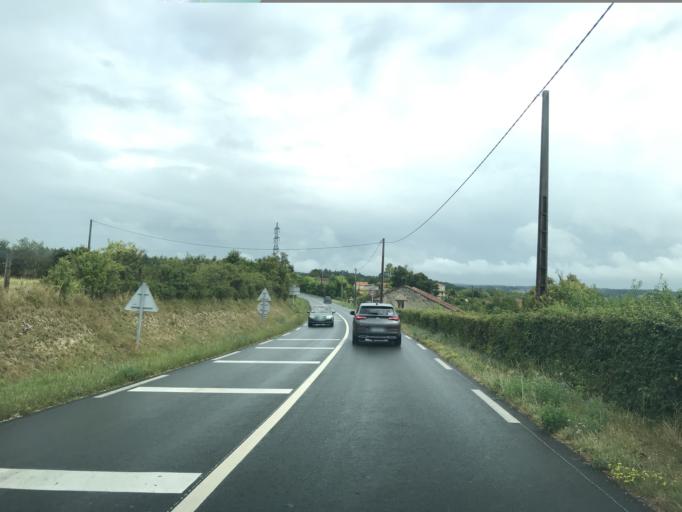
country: FR
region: Aquitaine
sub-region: Departement de la Dordogne
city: Coulounieix-Chamiers
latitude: 45.1571
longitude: 0.6986
